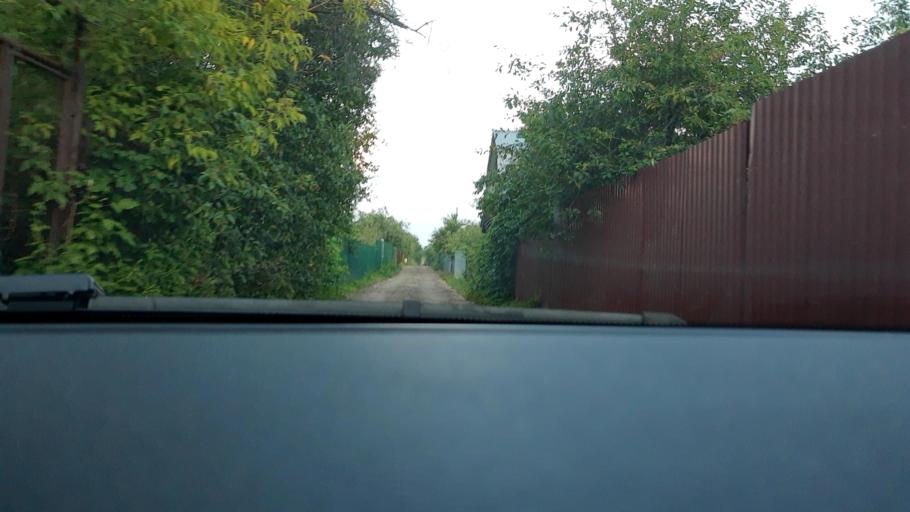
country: RU
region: Nizjnij Novgorod
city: Kstovo
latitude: 56.1560
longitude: 44.2563
